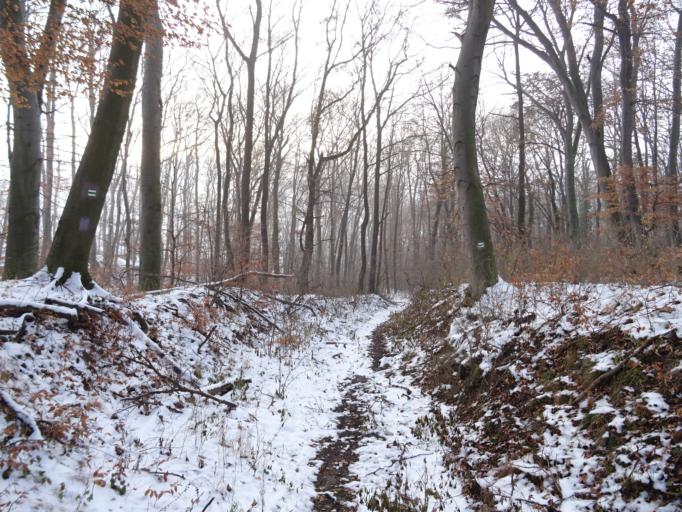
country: HU
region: Fejer
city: Mor
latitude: 47.3811
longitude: 18.2435
